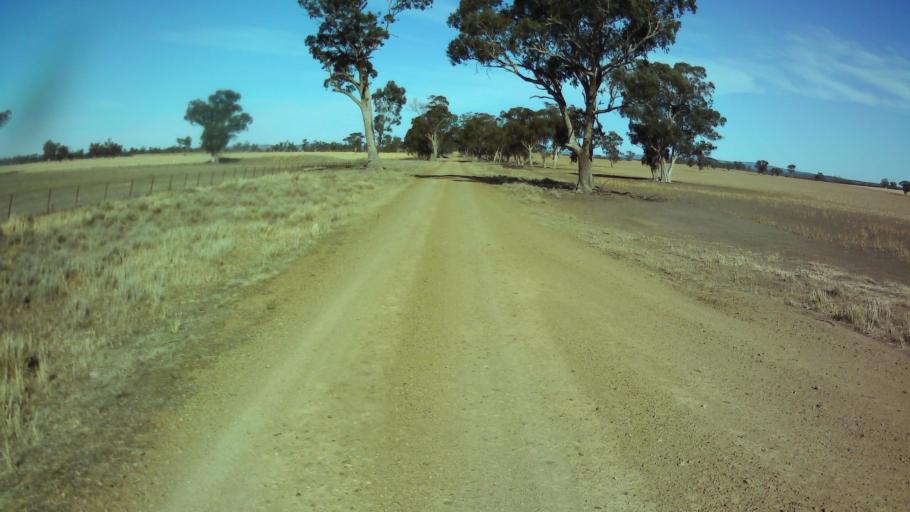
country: AU
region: New South Wales
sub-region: Weddin
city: Grenfell
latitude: -33.6598
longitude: 148.1115
